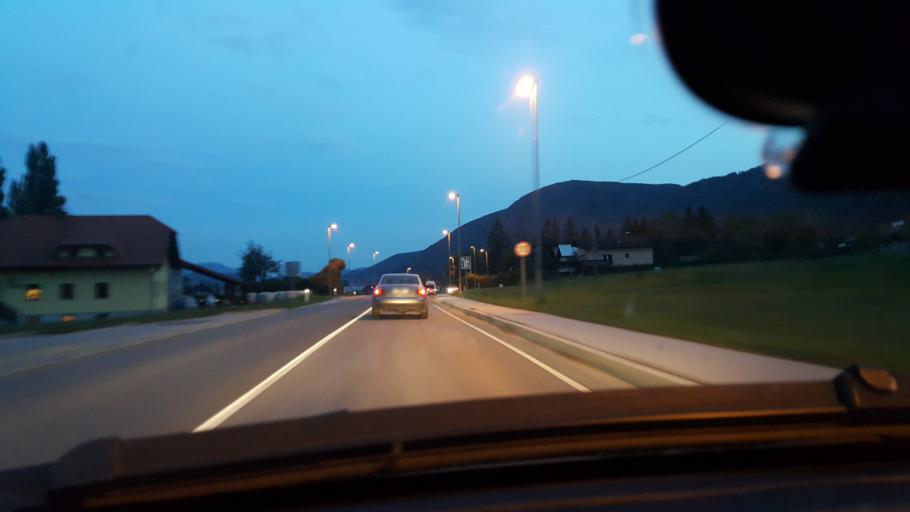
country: SI
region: Slovenska Konjice
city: Slovenske Konjice
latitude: 46.3462
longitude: 15.4085
